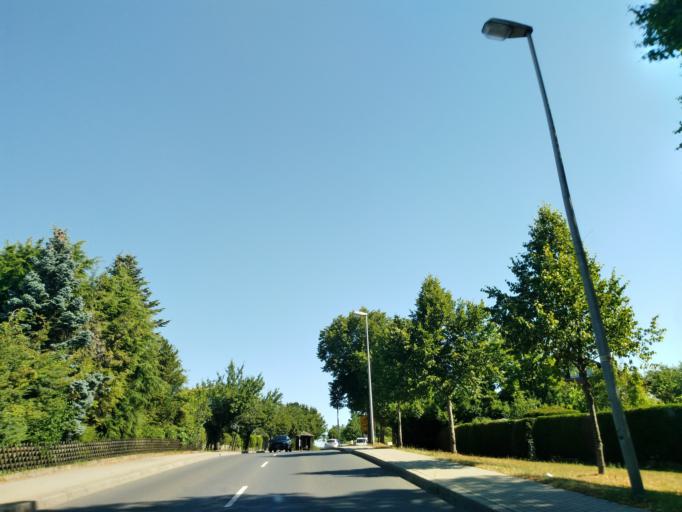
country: DE
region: Baden-Wuerttemberg
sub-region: Karlsruhe Region
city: Buchen
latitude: 49.5271
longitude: 9.3298
